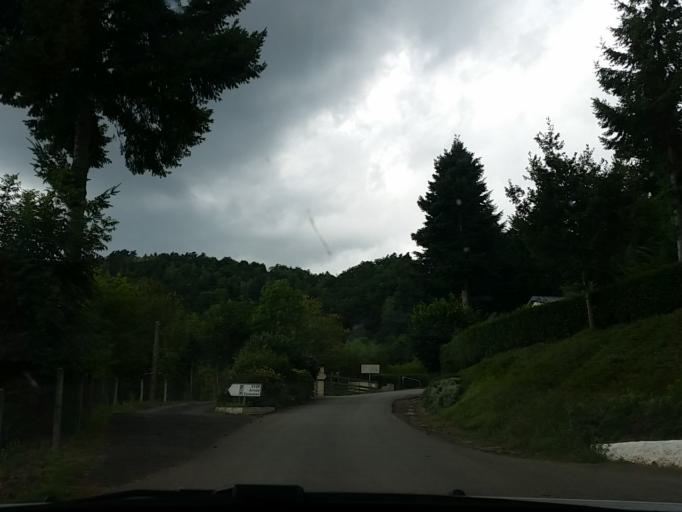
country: FR
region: Auvergne
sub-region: Departement du Cantal
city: Neuveglise
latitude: 44.8953
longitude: 3.0008
